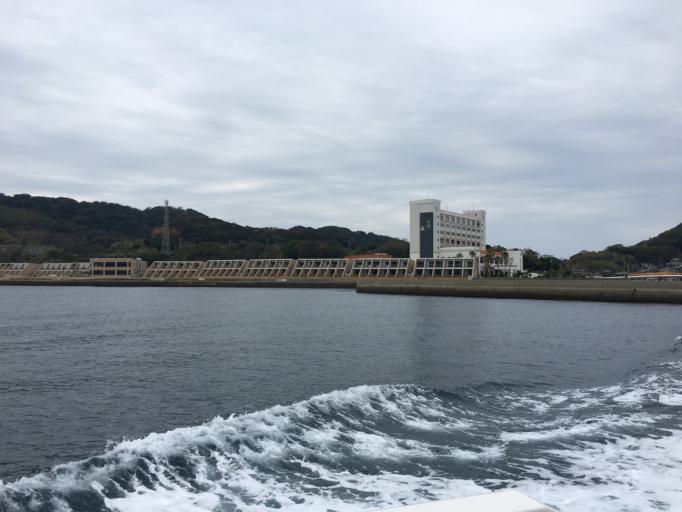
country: JP
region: Nagasaki
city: Nagasaki-shi
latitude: 32.7024
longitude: 129.7827
